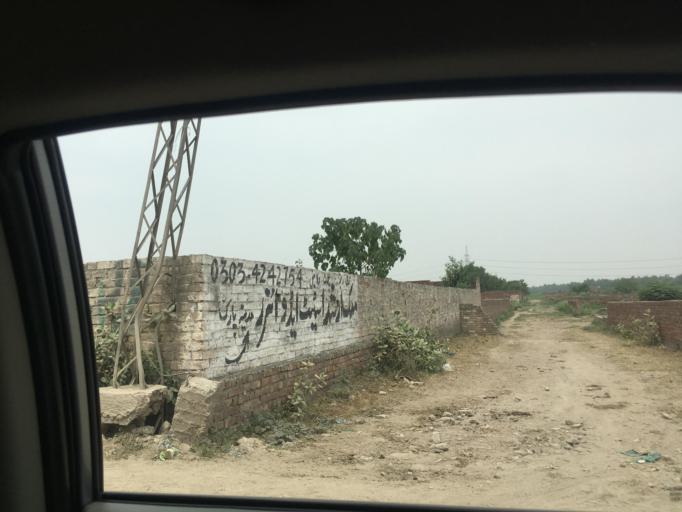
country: PK
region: Punjab
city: Lahore
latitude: 31.6198
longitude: 74.3529
